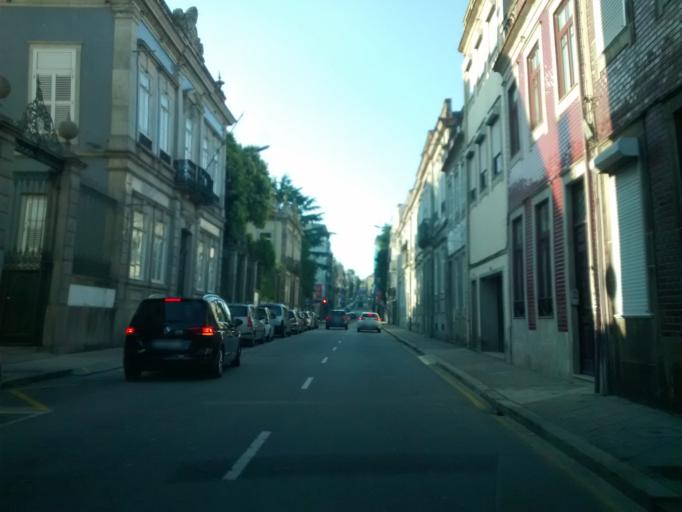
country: PT
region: Porto
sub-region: Porto
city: Porto
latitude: 41.1481
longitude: -8.6020
